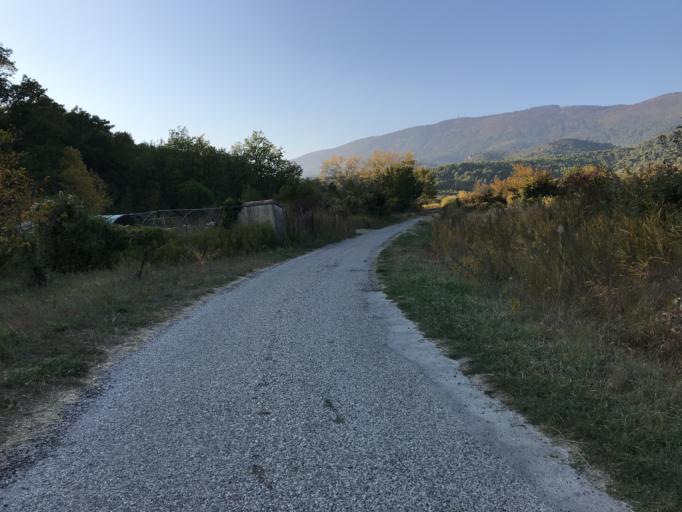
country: FR
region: Provence-Alpes-Cote d'Azur
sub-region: Departement du Vaucluse
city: Ansouis
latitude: 43.7861
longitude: 5.4976
